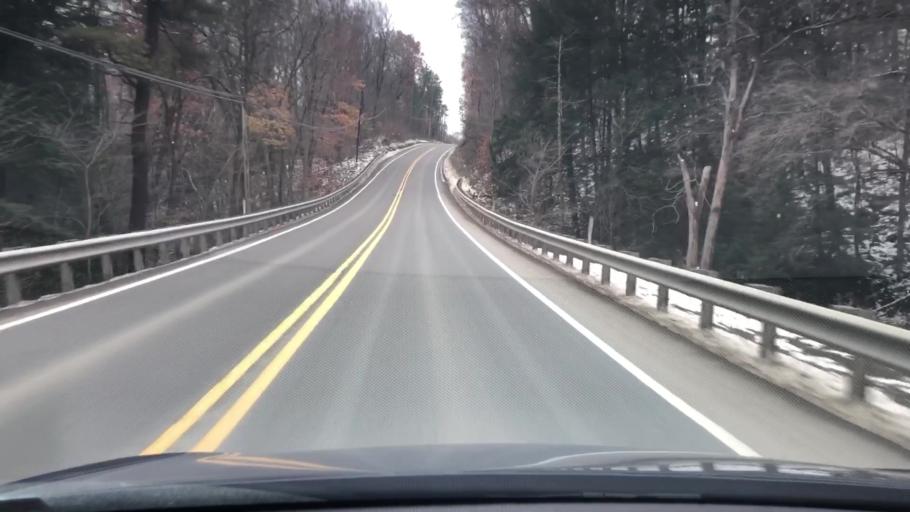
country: US
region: Pennsylvania
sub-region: Jefferson County
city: Brookville
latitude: 41.0371
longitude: -79.2588
